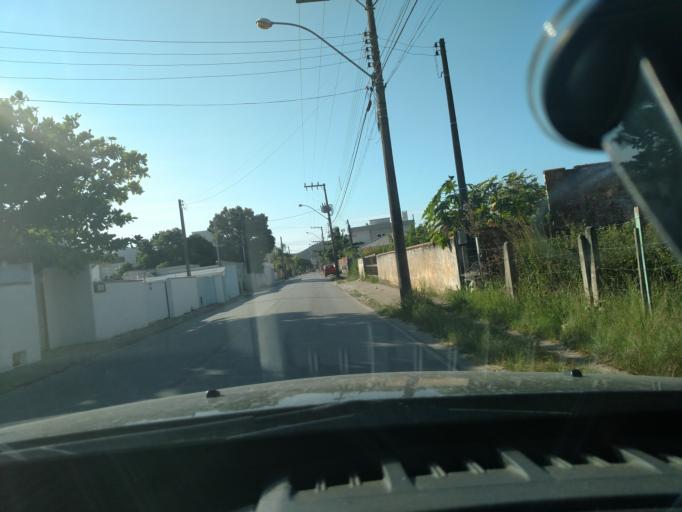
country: BR
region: Santa Catarina
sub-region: Porto Belo
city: Porto Belo
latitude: -27.1947
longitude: -48.5017
